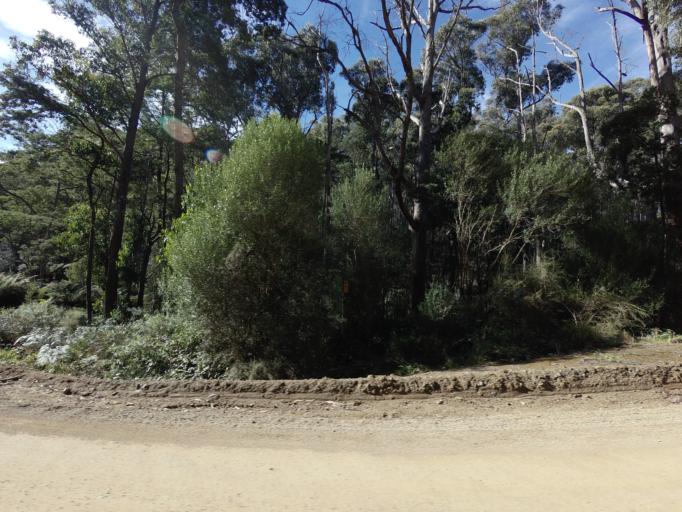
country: AU
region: Tasmania
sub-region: Clarence
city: Sandford
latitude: -43.1318
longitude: 147.7658
